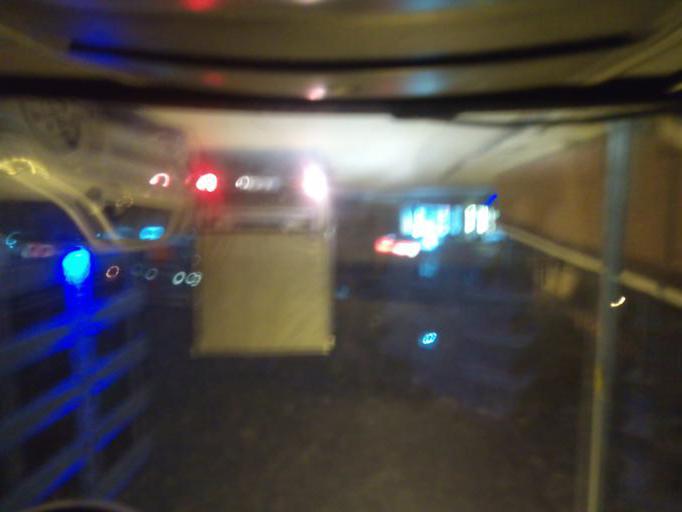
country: TR
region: Bursa
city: Niluefer
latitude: 40.2609
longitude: 28.9601
